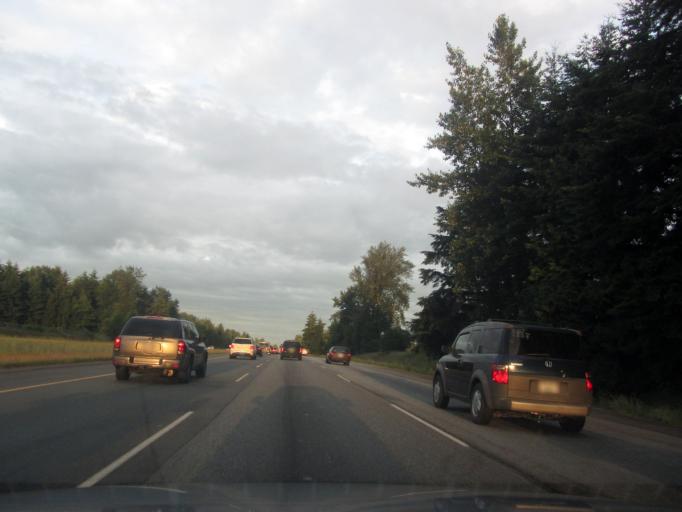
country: CA
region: British Columbia
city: Langley
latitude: 49.1173
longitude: -122.5334
